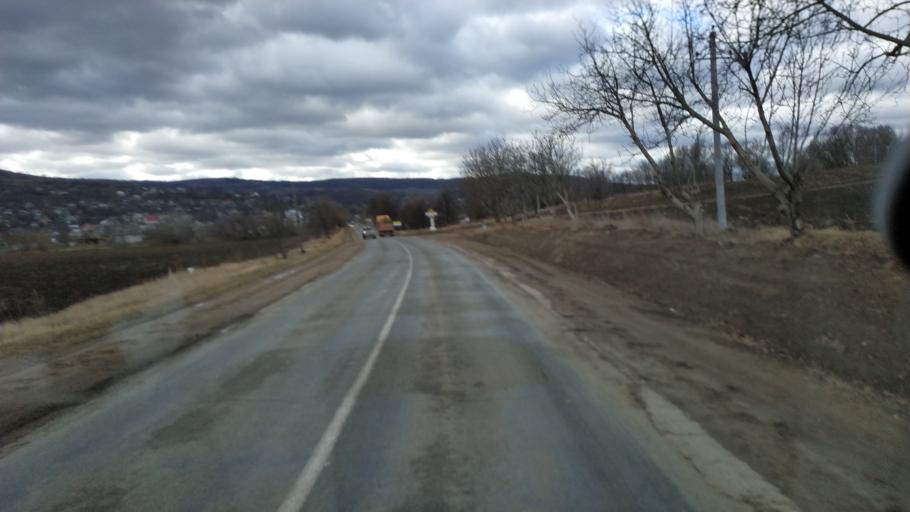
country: MD
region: Stinga Nistrului
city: Bucovat
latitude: 47.1656
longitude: 28.4366
